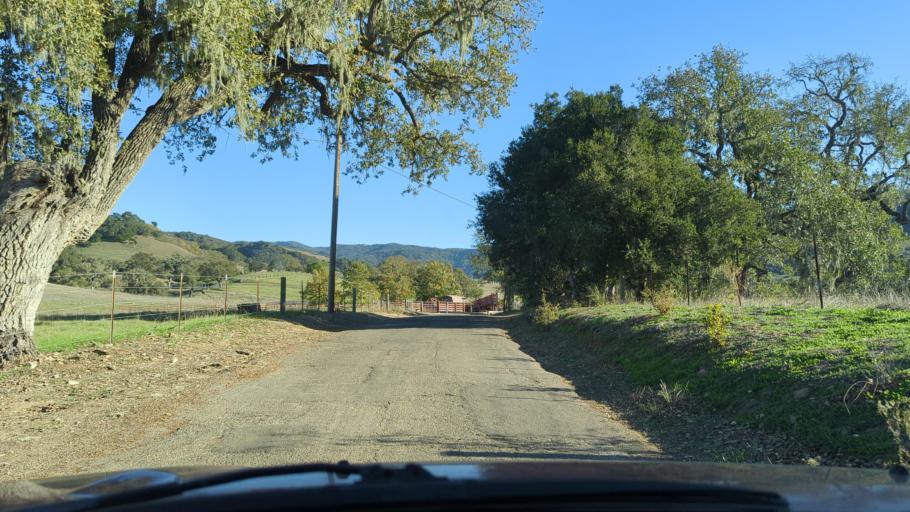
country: US
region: California
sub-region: Santa Barbara County
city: Santa Ynez
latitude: 34.5720
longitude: -120.0971
